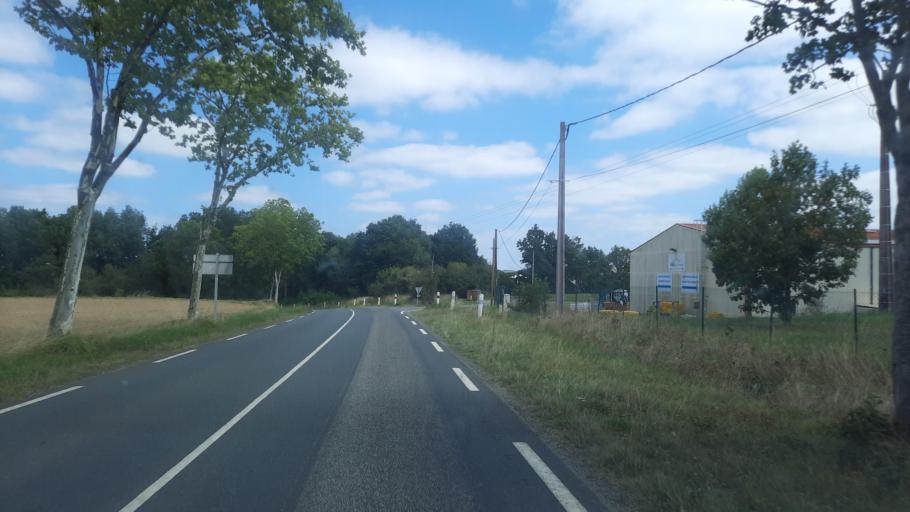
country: FR
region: Midi-Pyrenees
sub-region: Departement de la Haute-Garonne
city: Boulogne-sur-Gesse
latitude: 43.2927
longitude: 0.6592
